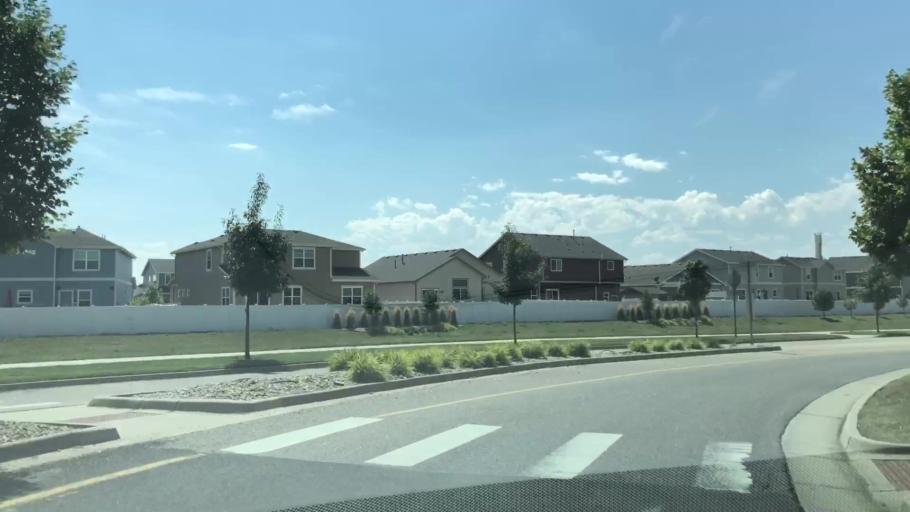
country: US
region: Colorado
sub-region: Larimer County
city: Loveland
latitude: 40.4044
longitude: -105.0356
